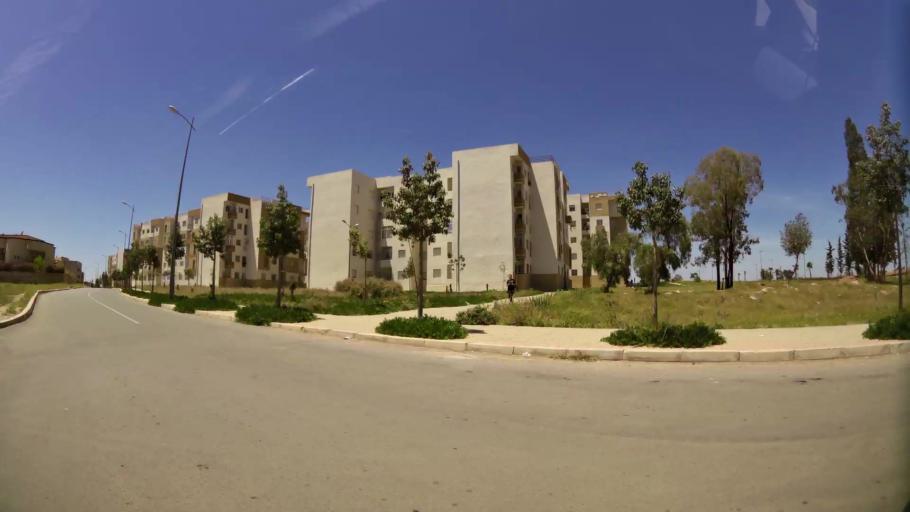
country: MA
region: Oriental
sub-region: Oujda-Angad
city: Oujda
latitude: 34.6647
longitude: -1.9200
